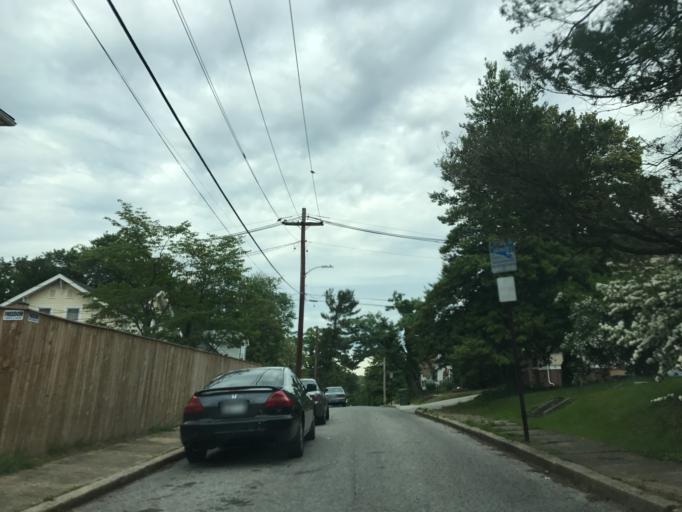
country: US
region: Maryland
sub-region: Baltimore County
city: Parkville
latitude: 39.3498
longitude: -76.5713
